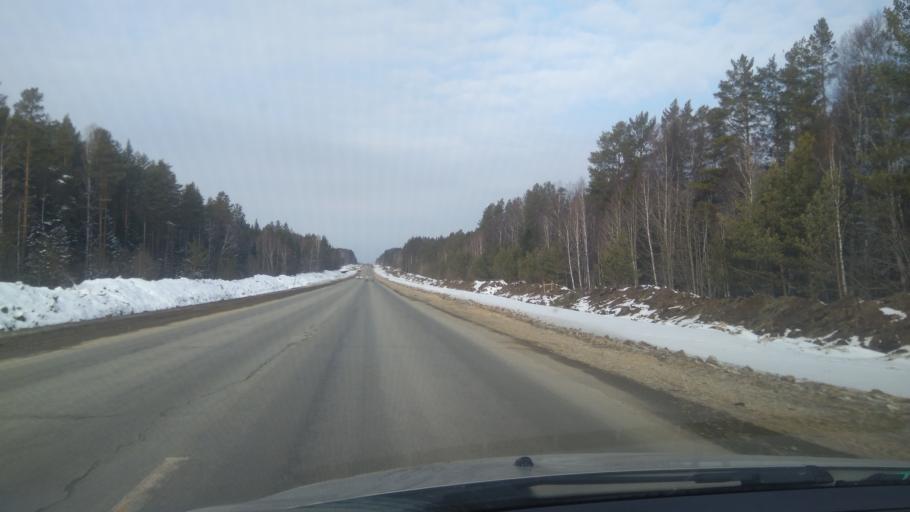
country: RU
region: Sverdlovsk
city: Bisert'
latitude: 56.8290
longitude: 58.9710
